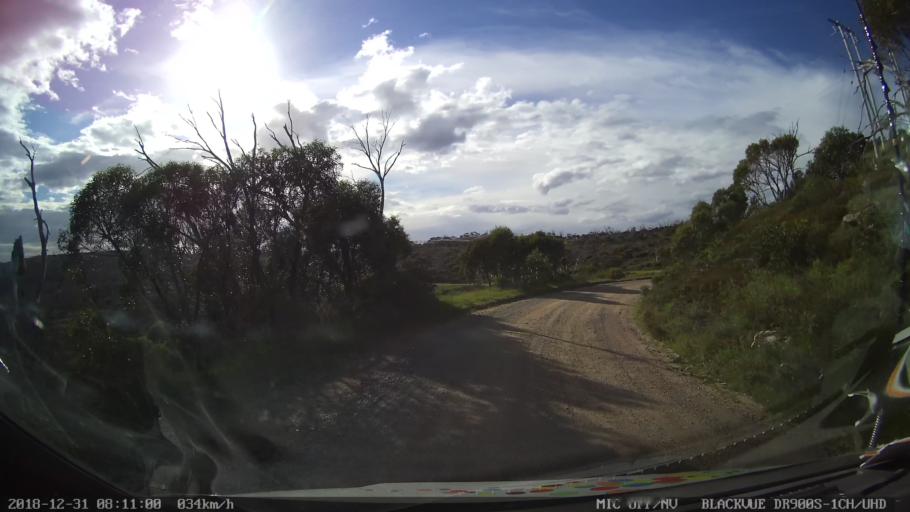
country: AU
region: New South Wales
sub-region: Snowy River
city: Jindabyne
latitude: -36.3847
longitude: 148.4241
